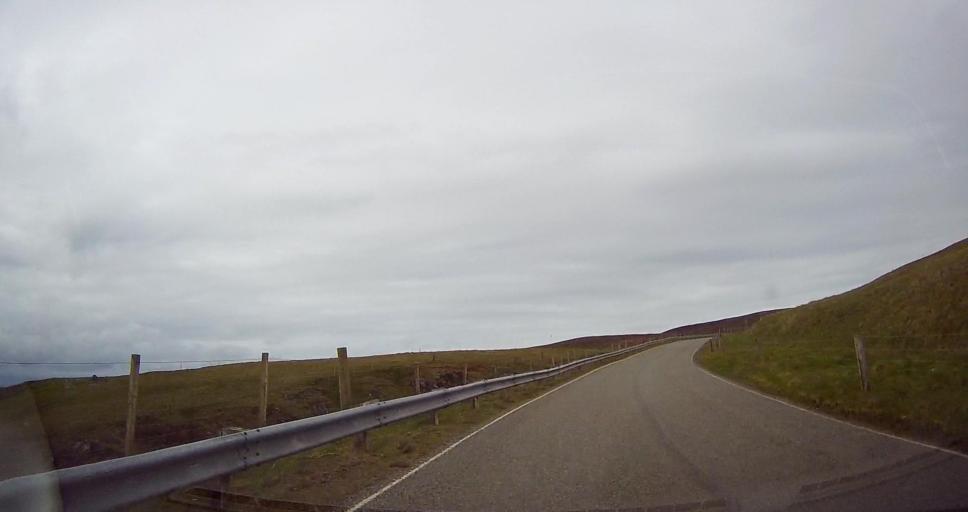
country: GB
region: Scotland
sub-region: Shetland Islands
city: Lerwick
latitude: 60.4851
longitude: -1.5026
